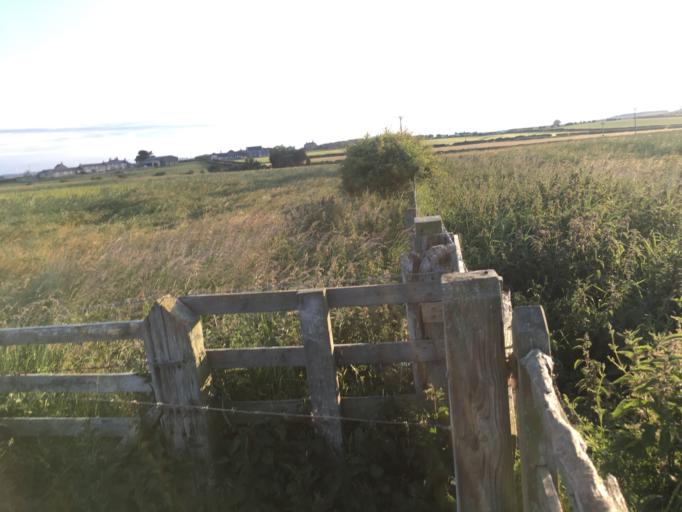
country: GB
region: England
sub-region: Northumberland
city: North Sunderland
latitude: 55.5821
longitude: -1.6730
